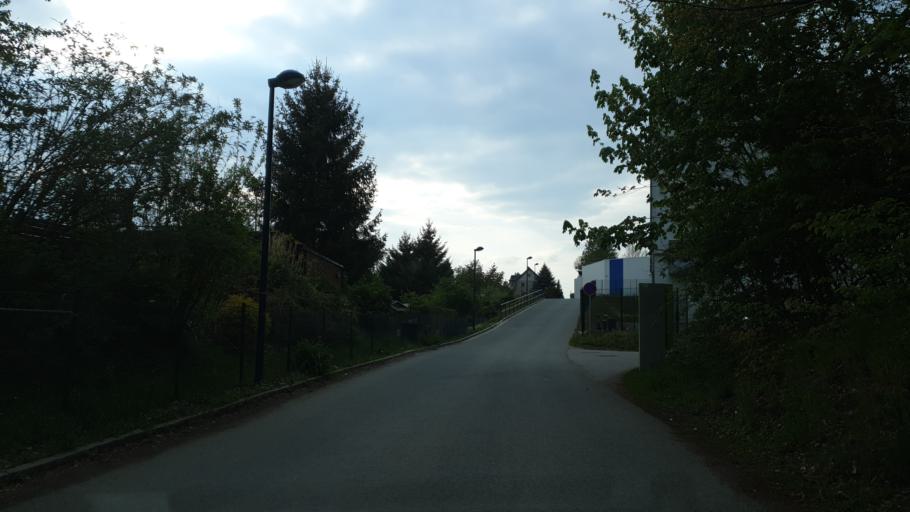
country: DE
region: Saxony
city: Oelsnitz
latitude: 50.7309
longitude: 12.7050
